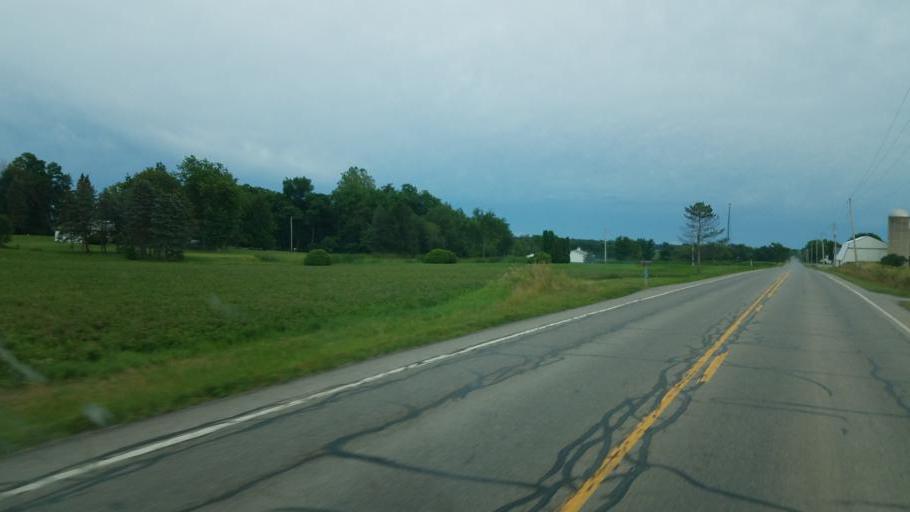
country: US
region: Ohio
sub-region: Huron County
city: Greenwich
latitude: 40.9256
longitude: -82.4973
